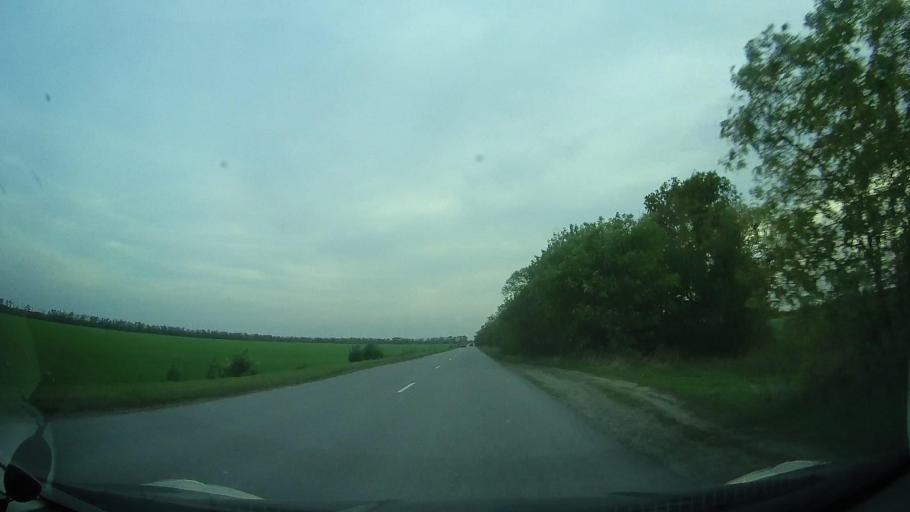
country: RU
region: Rostov
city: Kirovskaya
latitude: 47.0102
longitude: 39.9788
